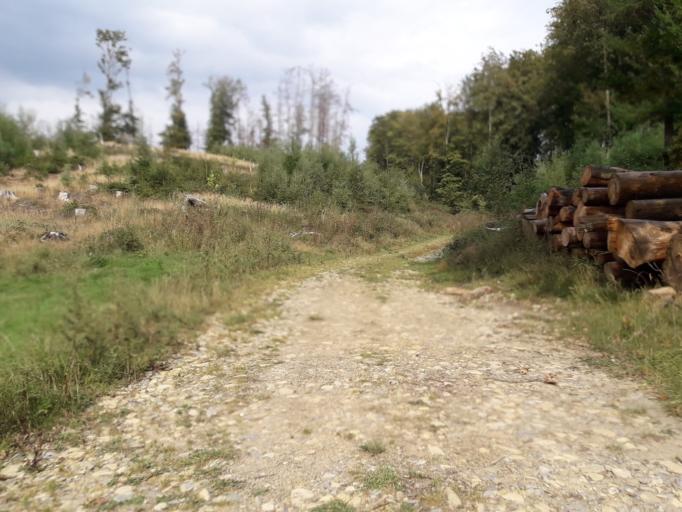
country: DE
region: North Rhine-Westphalia
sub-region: Regierungsbezirk Detmold
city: Schlangen
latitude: 51.8332
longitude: 8.8726
